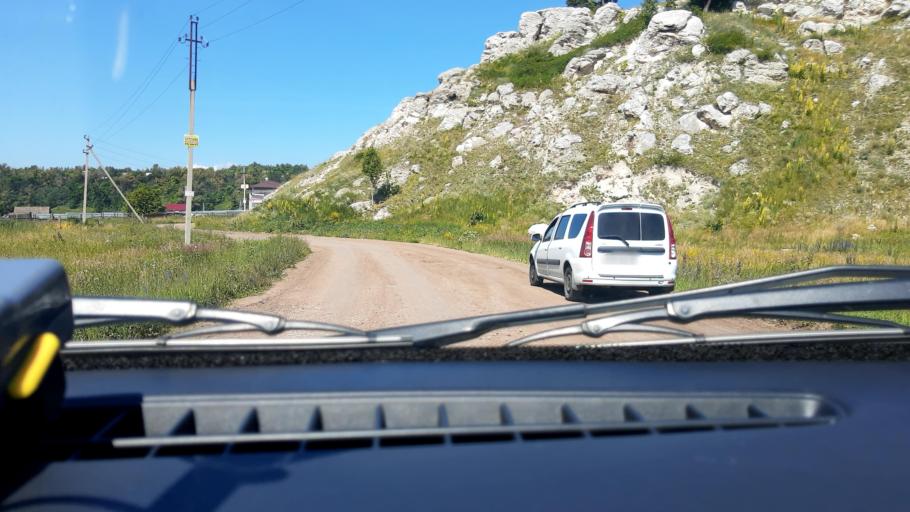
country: RU
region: Bashkortostan
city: Karmaskaly
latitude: 54.3592
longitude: 55.9012
